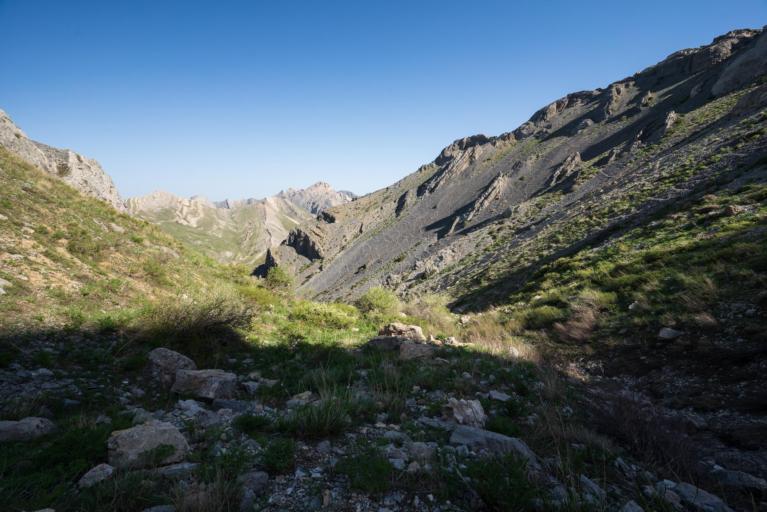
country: KZ
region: Ongtustik Qazaqstan
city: Kentau
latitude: 43.9308
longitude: 68.2900
